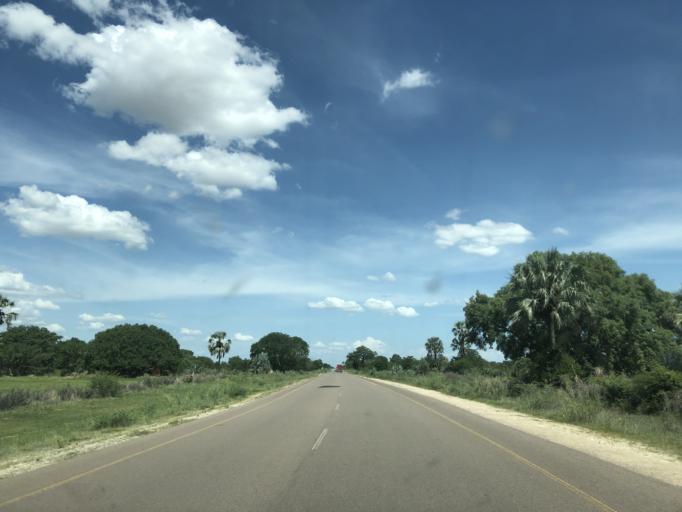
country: AO
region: Cunene
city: Ondjiva
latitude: -16.8900
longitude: 15.4943
